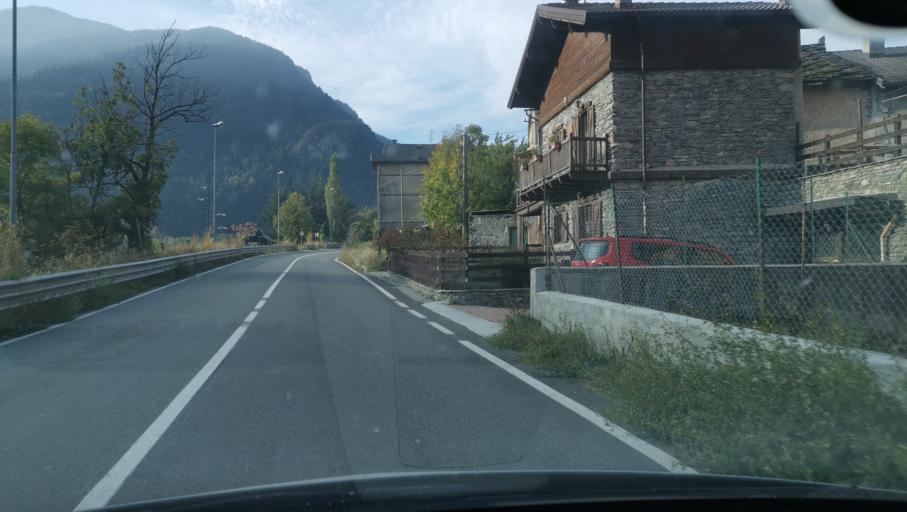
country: IT
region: Piedmont
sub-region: Provincia di Torino
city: Salbertrand
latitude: 45.0719
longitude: 6.8845
